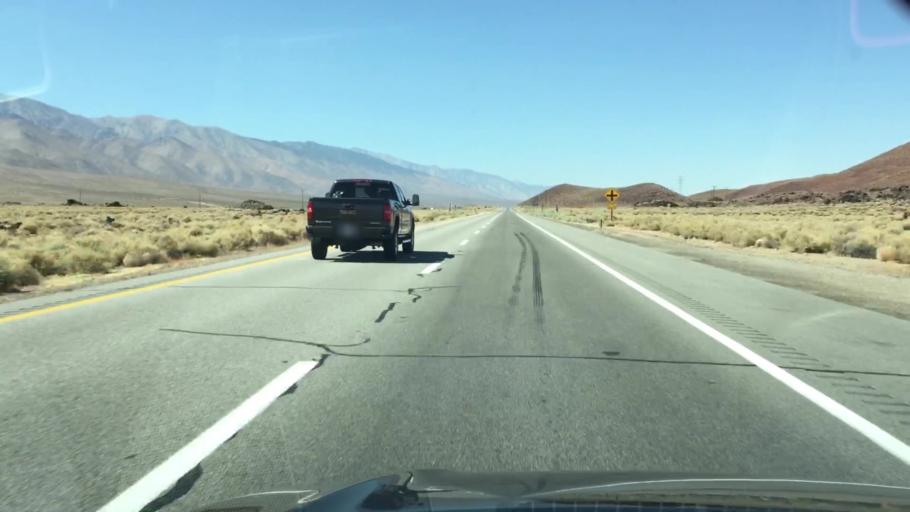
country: US
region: California
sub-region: Kern County
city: Inyokern
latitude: 35.9751
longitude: -117.9220
